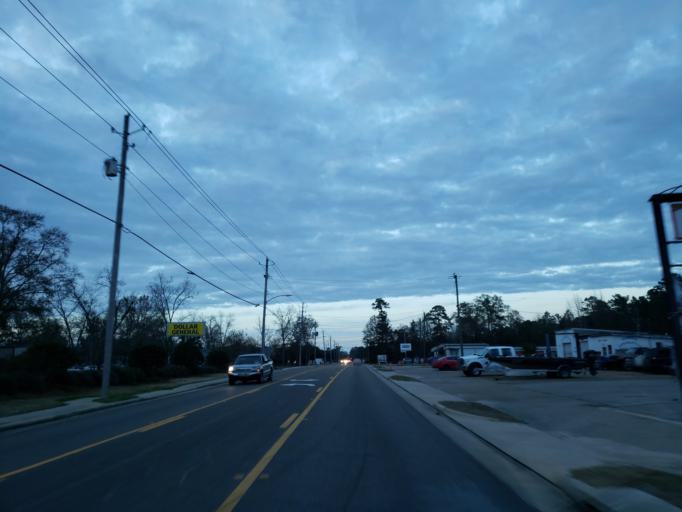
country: US
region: Mississippi
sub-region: Forrest County
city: Petal
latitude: 31.3341
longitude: -89.2629
